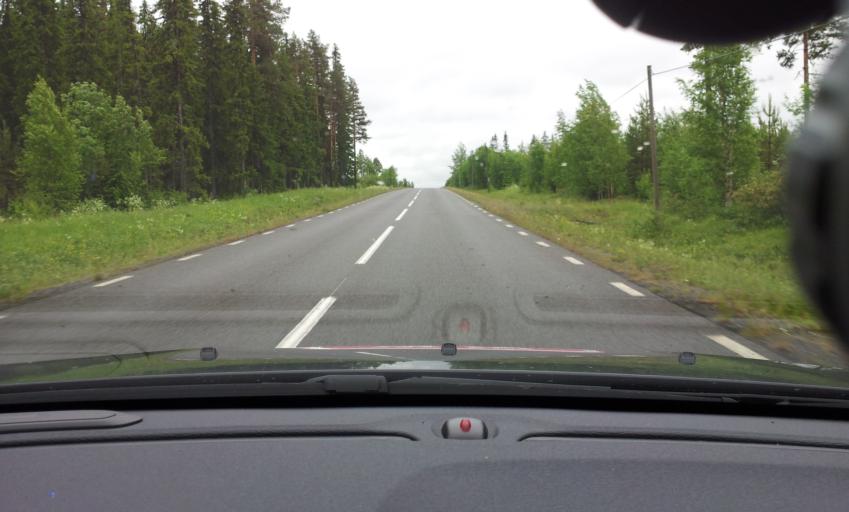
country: SE
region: Jaemtland
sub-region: OEstersunds Kommun
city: Lit
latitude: 63.7096
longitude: 14.9832
